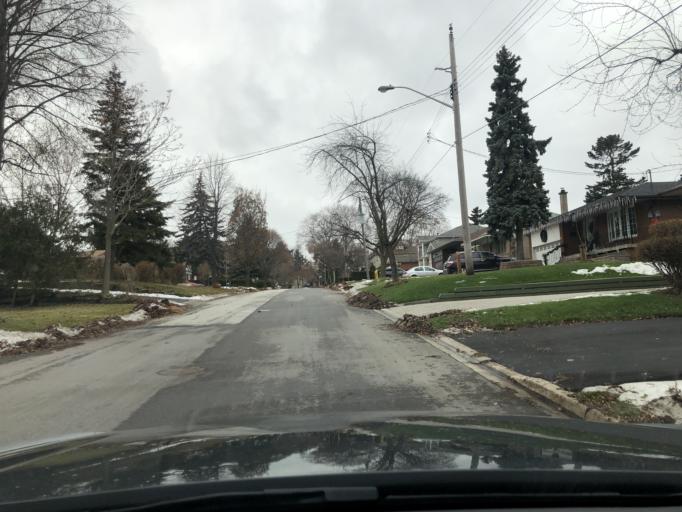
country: CA
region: Ontario
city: Etobicoke
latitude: 43.6923
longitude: -79.5184
